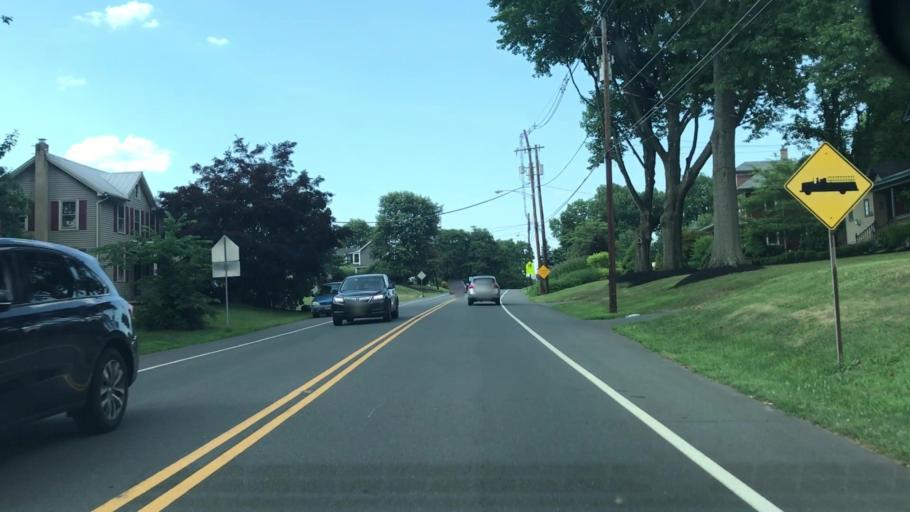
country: US
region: New Jersey
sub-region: Hunterdon County
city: Flemington
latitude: 40.5225
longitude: -74.7982
